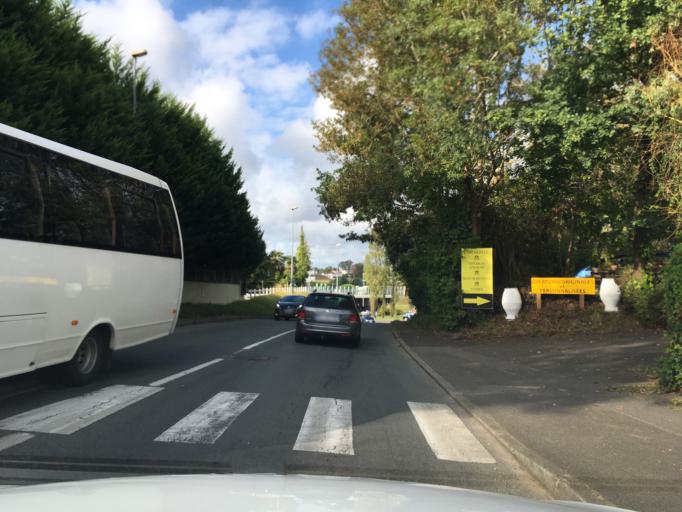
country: FR
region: Aquitaine
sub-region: Departement des Pyrenees-Atlantiques
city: Anglet
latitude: 43.4593
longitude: -1.4968
